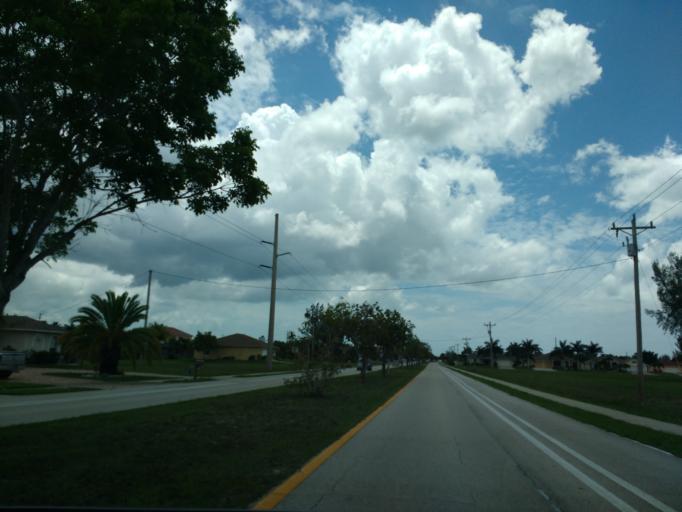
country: US
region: Florida
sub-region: Lee County
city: Cape Coral
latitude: 26.5668
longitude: -82.0173
